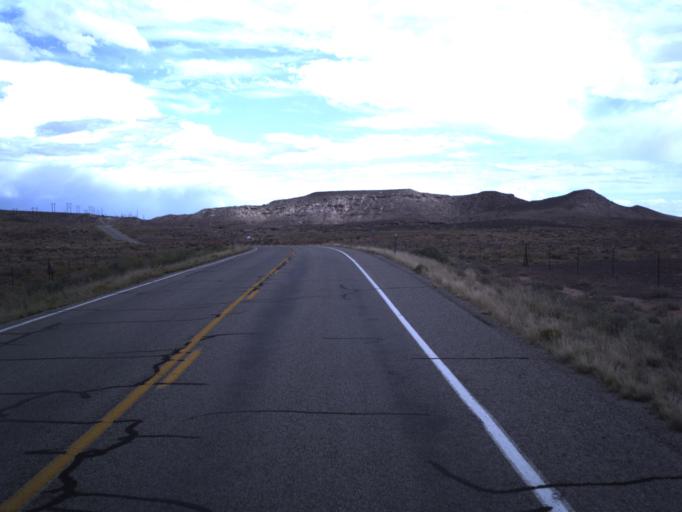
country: US
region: Utah
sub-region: San Juan County
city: Blanding
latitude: 37.2889
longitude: -109.3975
